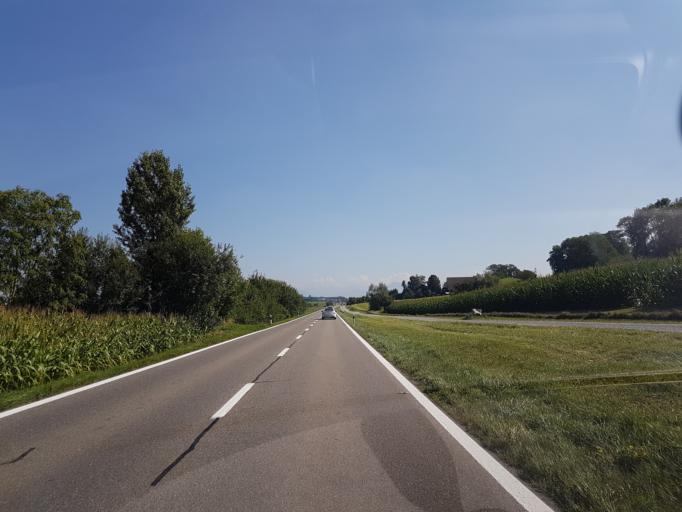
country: CH
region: Aargau
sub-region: Bezirk Muri
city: Waltenschwil
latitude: 47.3196
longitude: 8.3017
